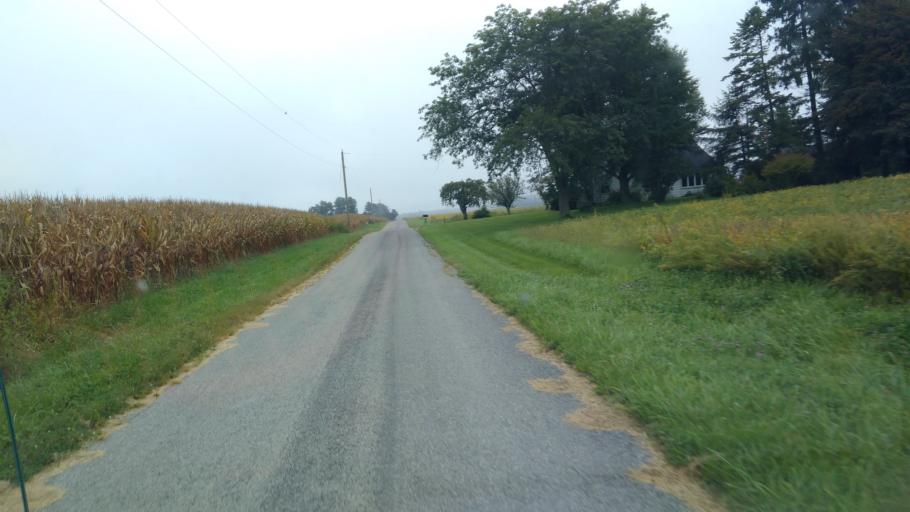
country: US
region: Ohio
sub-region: Union County
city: Richwood
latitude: 40.4999
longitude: -83.4150
